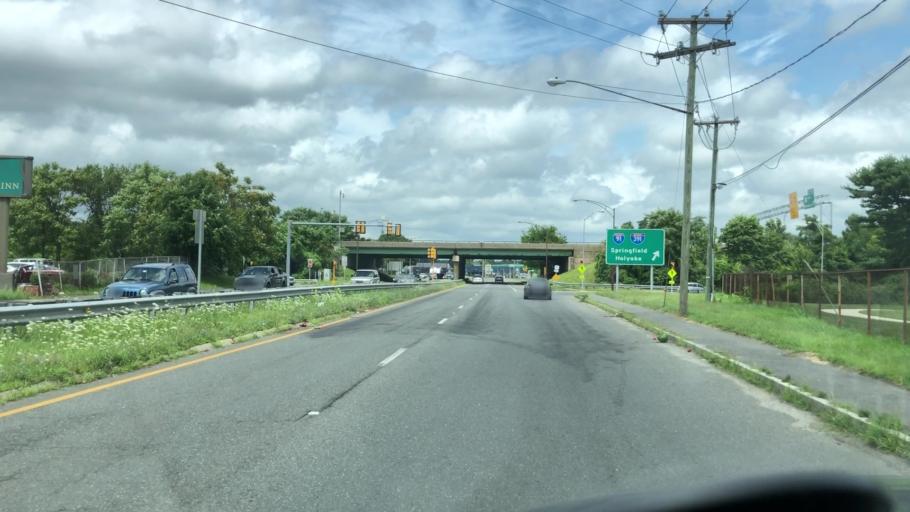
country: US
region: Massachusetts
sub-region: Hampden County
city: Chicopee
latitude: 42.1348
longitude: -72.6257
